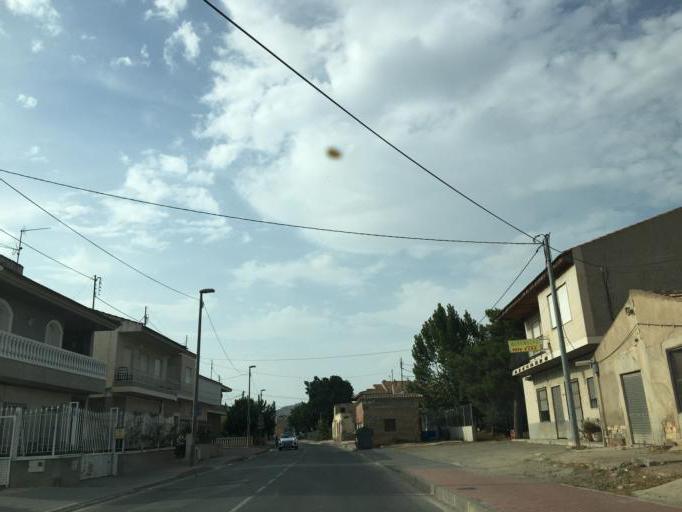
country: ES
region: Murcia
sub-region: Murcia
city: Murcia
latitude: 38.0071
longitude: -1.0793
